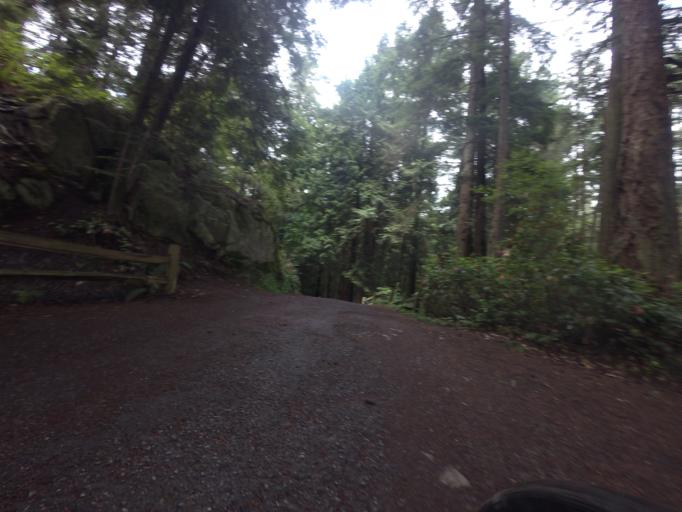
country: CA
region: British Columbia
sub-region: Greater Vancouver Regional District
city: Bowen Island
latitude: 49.3346
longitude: -123.2632
